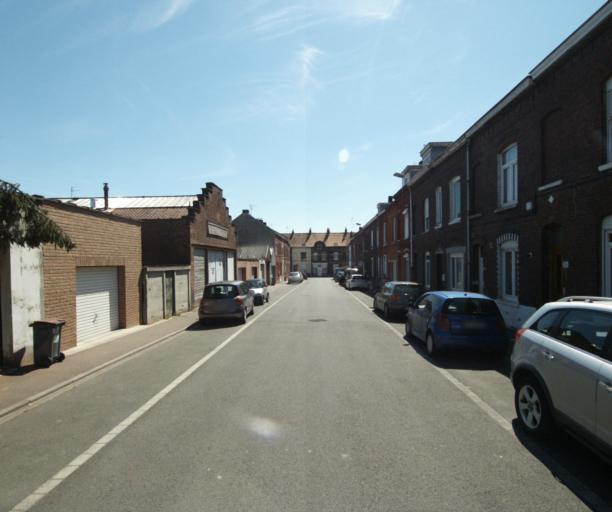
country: FR
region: Nord-Pas-de-Calais
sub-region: Departement du Nord
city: Tourcoing
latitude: 50.7288
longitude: 3.1709
